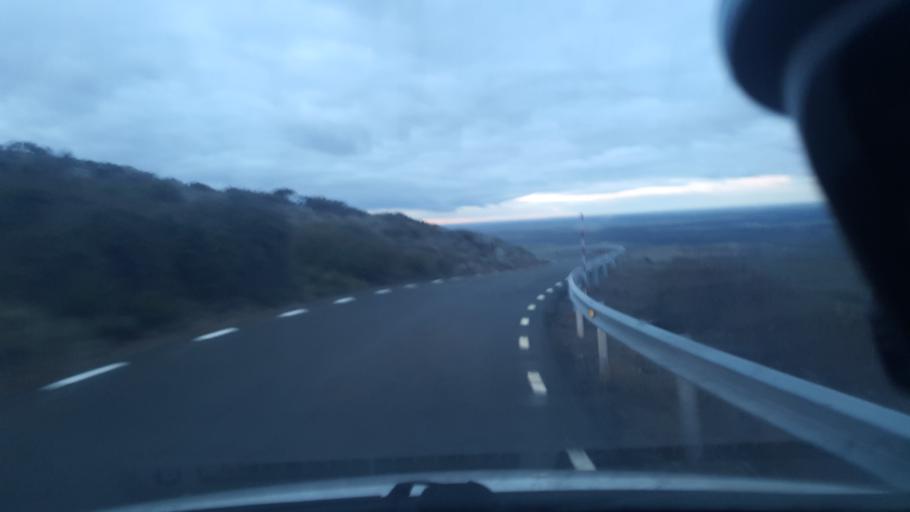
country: ES
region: Castille and Leon
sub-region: Provincia de Avila
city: Ojos-Albos
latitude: 40.7253
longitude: -4.4580
